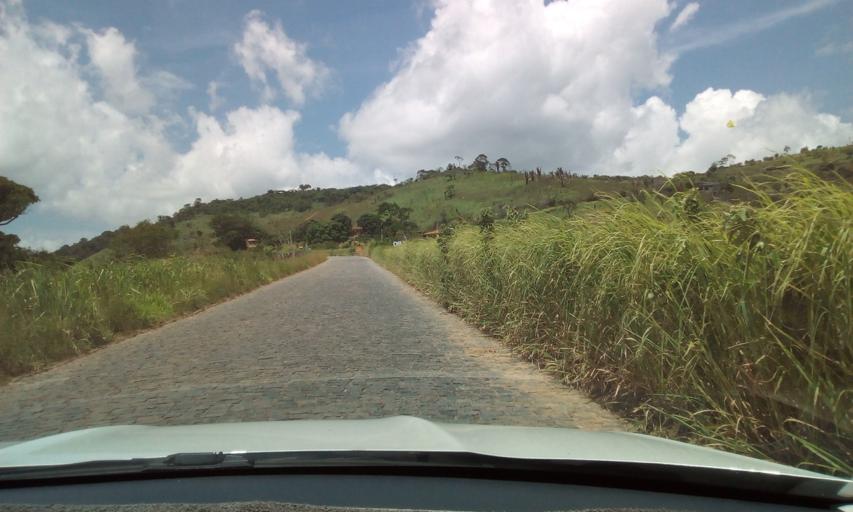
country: BR
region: Pernambuco
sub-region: Bonito
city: Bonito
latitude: -8.4913
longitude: -35.7269
